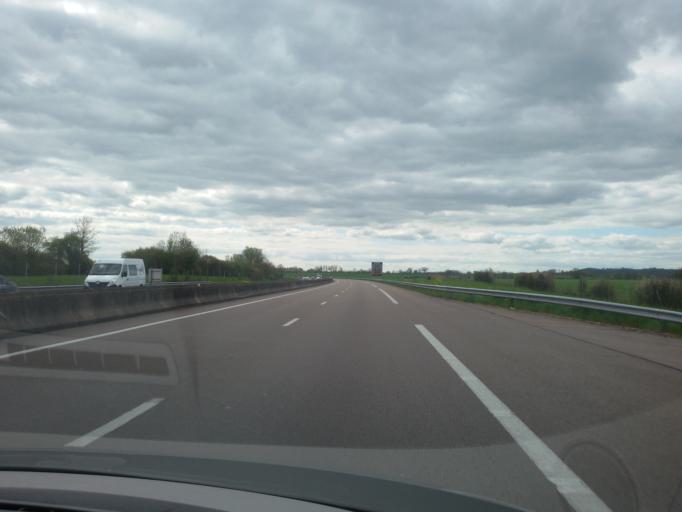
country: FR
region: Bourgogne
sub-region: Departement de la Cote-d'Or
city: Pouilly-en-Auxois
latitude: 47.2743
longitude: 4.5115
